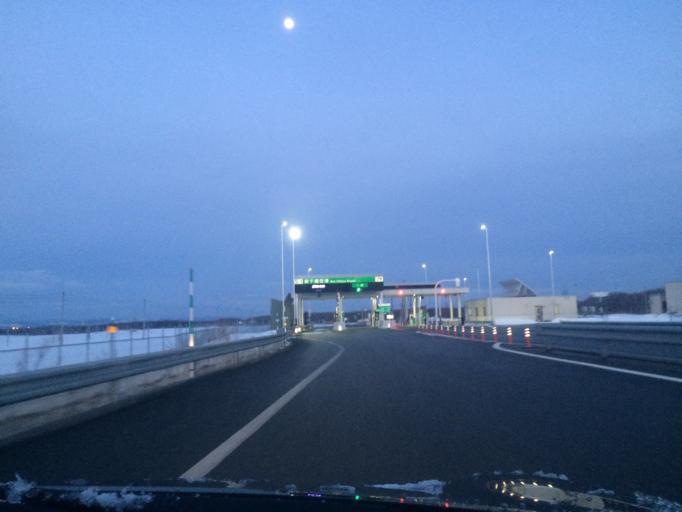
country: JP
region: Hokkaido
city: Chitose
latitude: 42.7769
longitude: 141.6313
